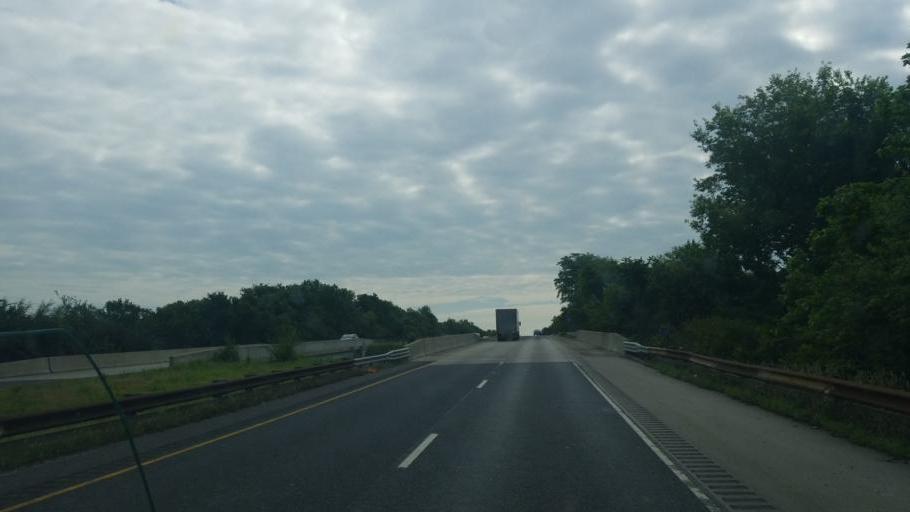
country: US
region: Indiana
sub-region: Vigo County
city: Terre Haute
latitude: 39.4308
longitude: -87.4075
